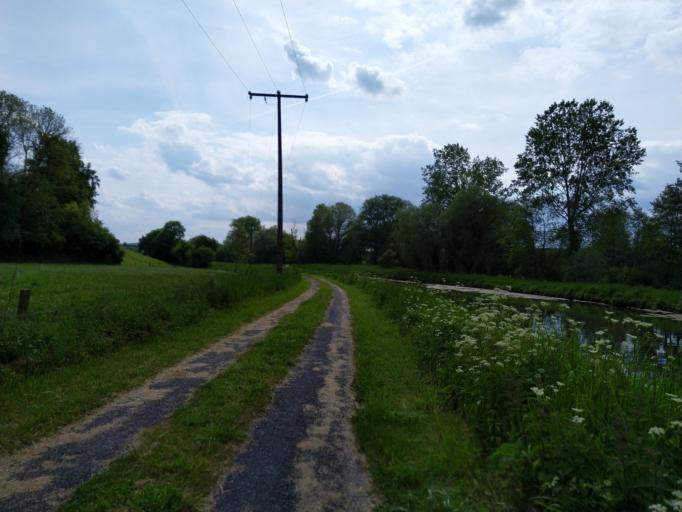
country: FR
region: Picardie
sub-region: Departement de l'Aisne
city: Guise
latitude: 49.9508
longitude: 3.5981
